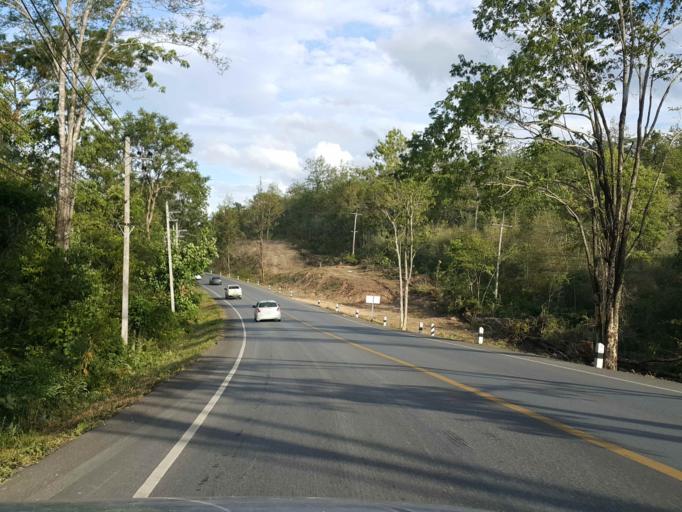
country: TH
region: Tak
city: Tak
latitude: 16.8034
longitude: 98.9982
